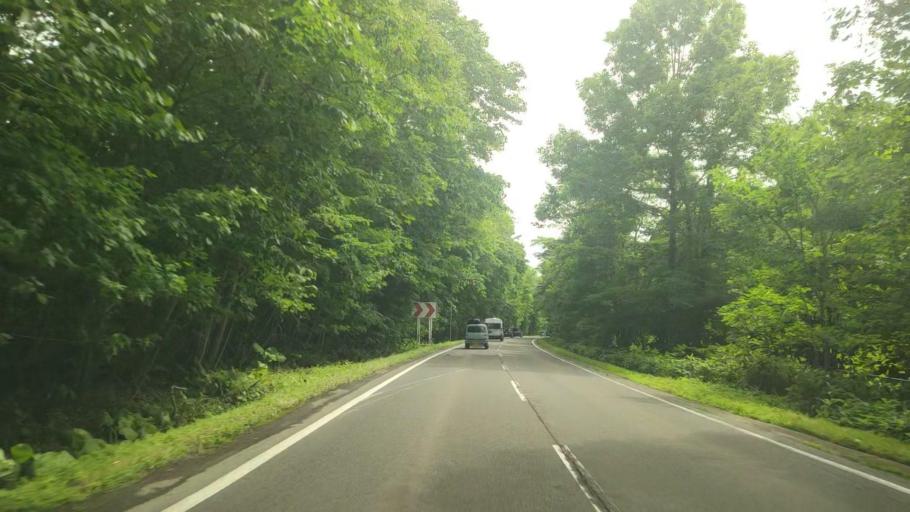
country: JP
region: Hokkaido
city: Tomakomai
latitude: 42.7754
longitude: 141.4407
